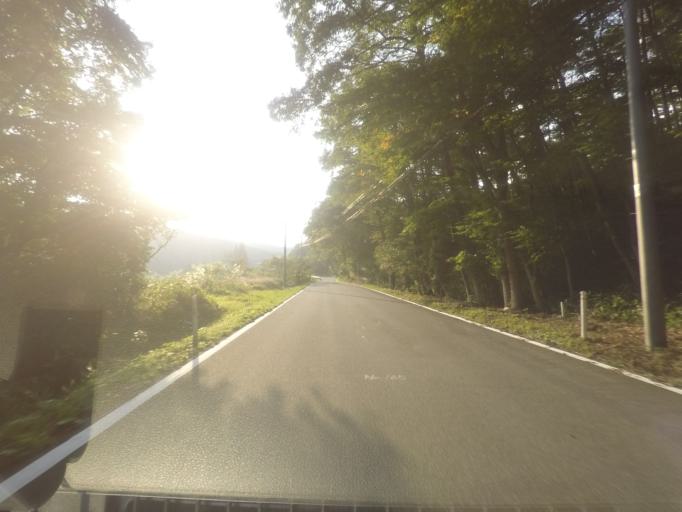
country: JP
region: Fukushima
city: Namie
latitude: 37.5631
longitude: 140.8095
